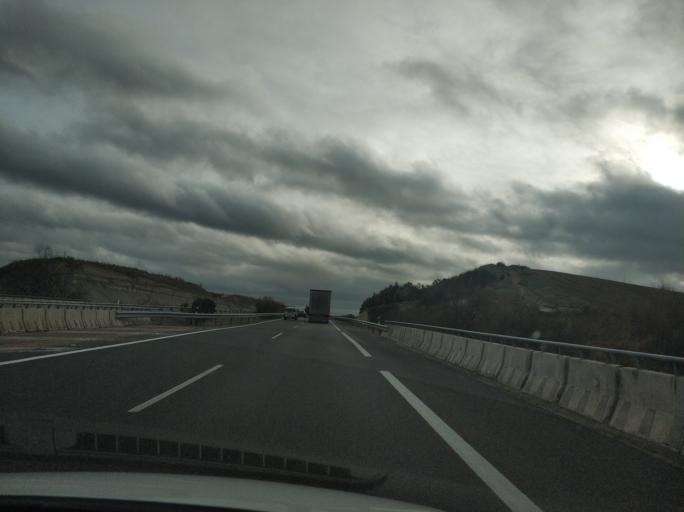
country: ES
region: Castille and Leon
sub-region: Provincia de Palencia
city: Soto de Cerrato
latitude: 41.9625
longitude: -4.4575
